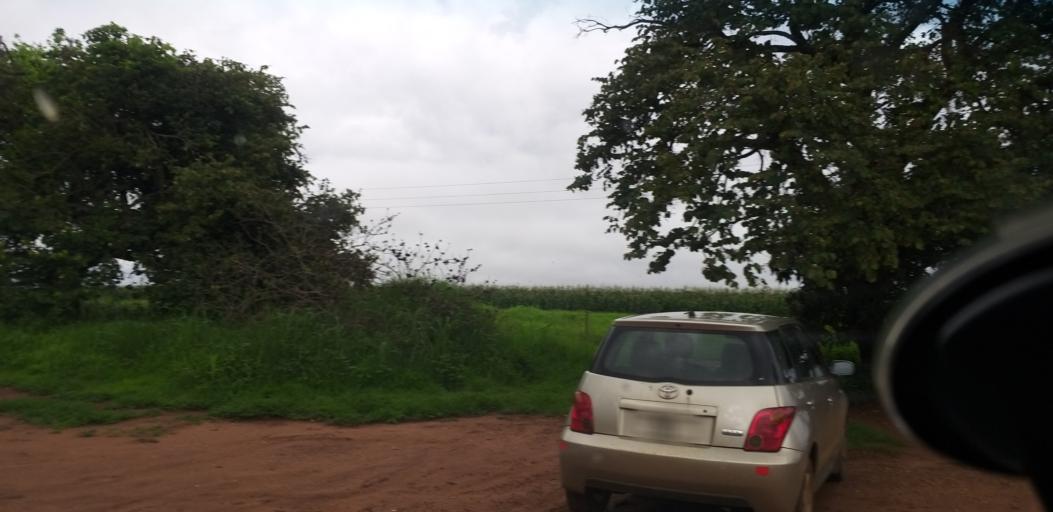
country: ZM
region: Lusaka
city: Lusaka
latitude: -15.5301
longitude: 28.3103
